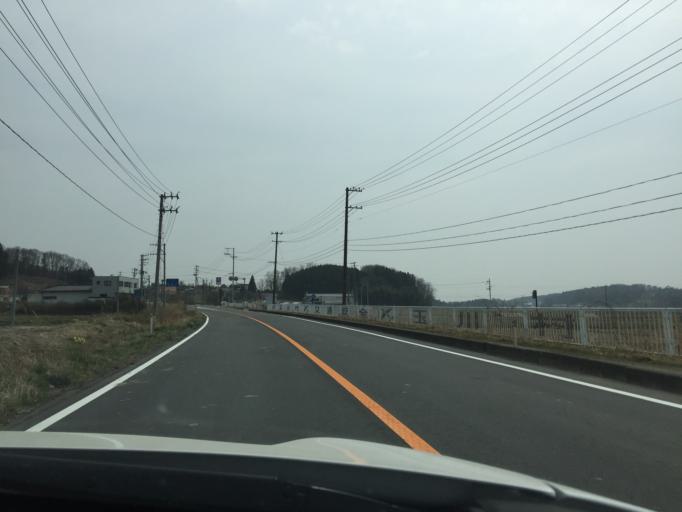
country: JP
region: Fukushima
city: Ishikawa
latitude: 37.1945
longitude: 140.4091
